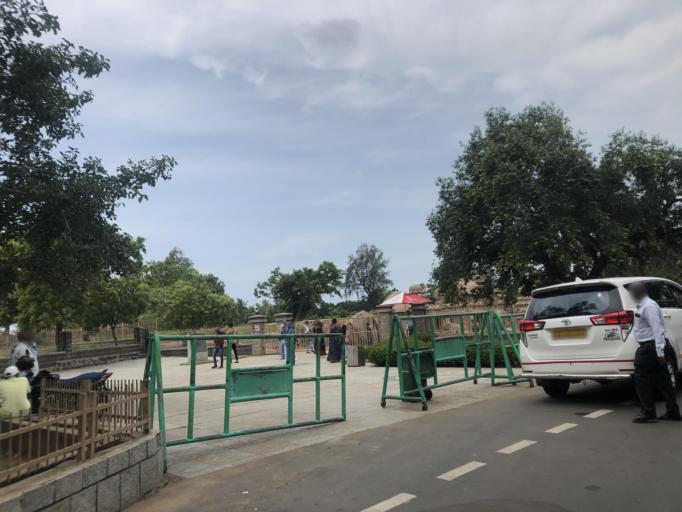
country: IN
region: Tamil Nadu
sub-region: Kancheepuram
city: Mamallapuram
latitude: 12.6097
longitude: 80.1898
